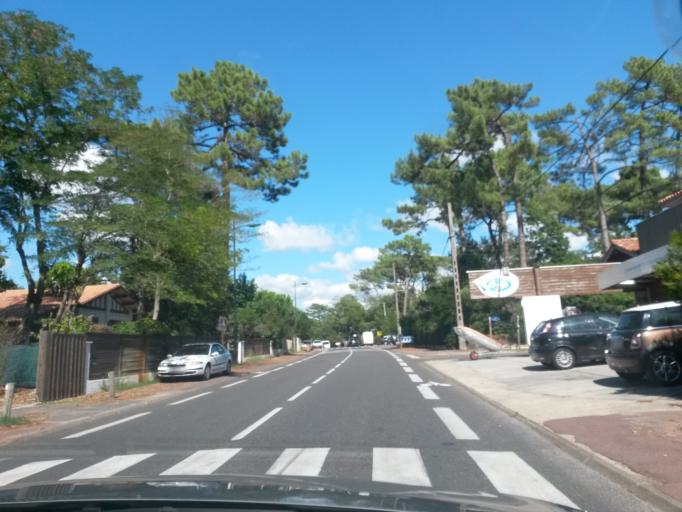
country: FR
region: Aquitaine
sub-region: Departement de la Gironde
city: Arcachon
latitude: 44.7148
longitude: -1.2144
